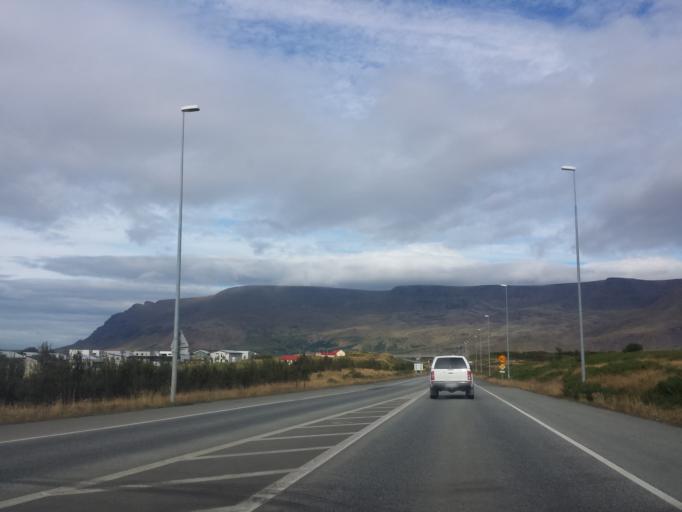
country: IS
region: Capital Region
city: Mosfellsbaer
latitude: 64.1779
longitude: -21.6775
